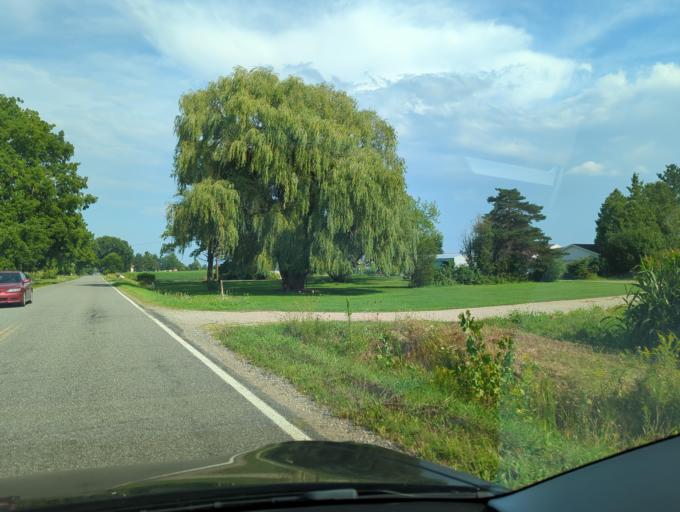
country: US
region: Michigan
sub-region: Ionia County
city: Ionia
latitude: 42.9297
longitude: -85.1026
